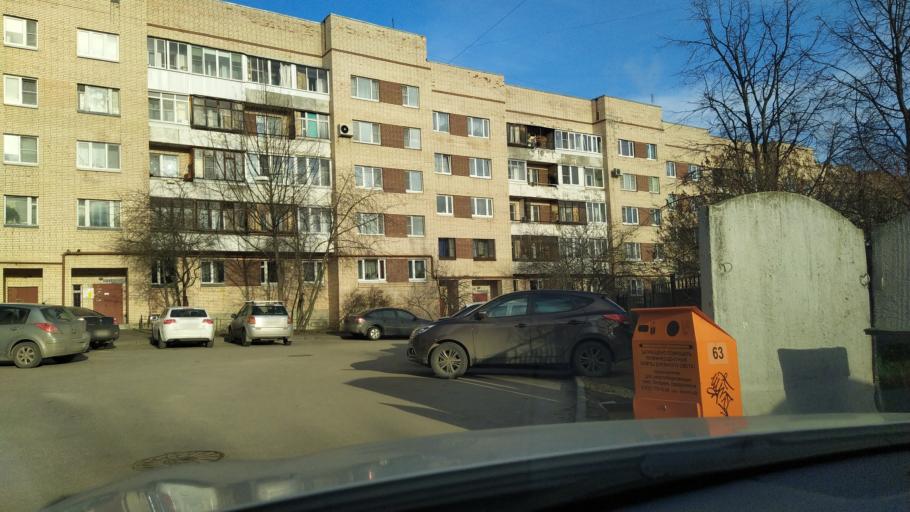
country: RU
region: St.-Petersburg
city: Pushkin
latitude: 59.7371
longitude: 30.4021
